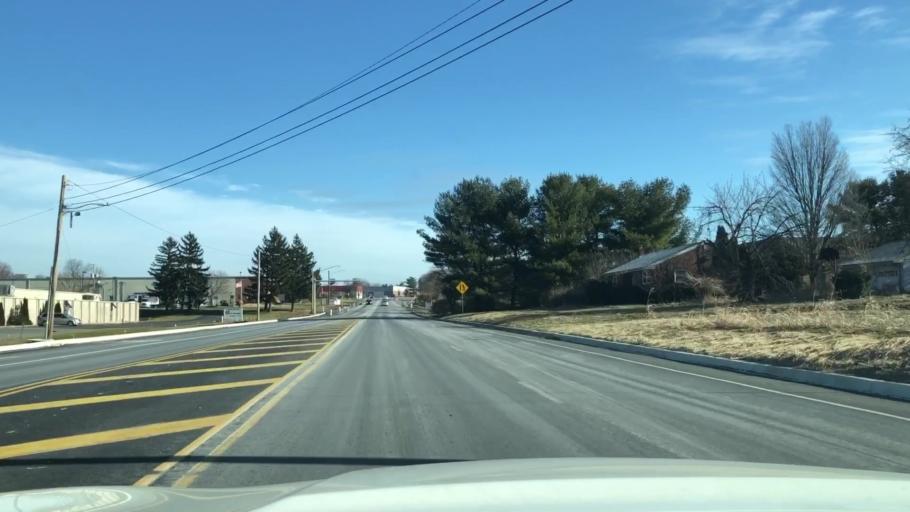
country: US
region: Pennsylvania
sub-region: Lehigh County
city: Catasauqua
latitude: 40.6586
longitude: -75.4451
